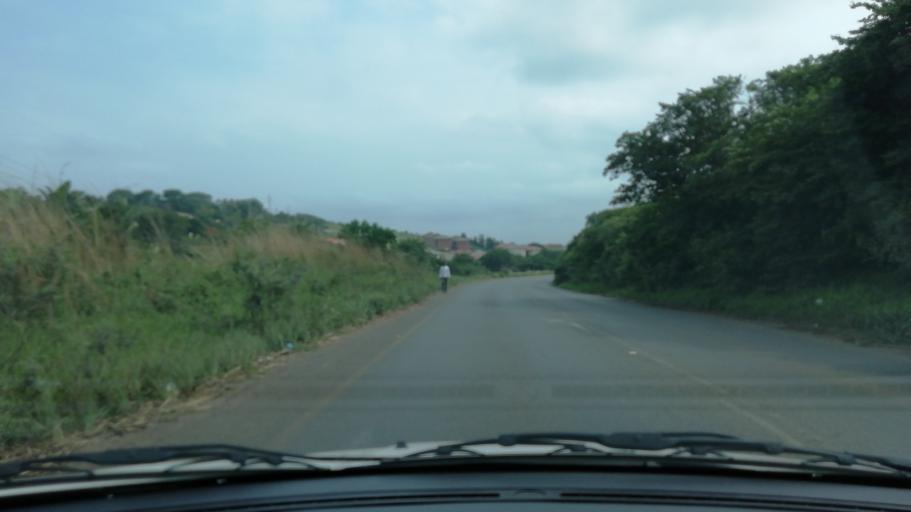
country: ZA
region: KwaZulu-Natal
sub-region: uThungulu District Municipality
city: Empangeni
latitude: -28.7468
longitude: 31.8806
